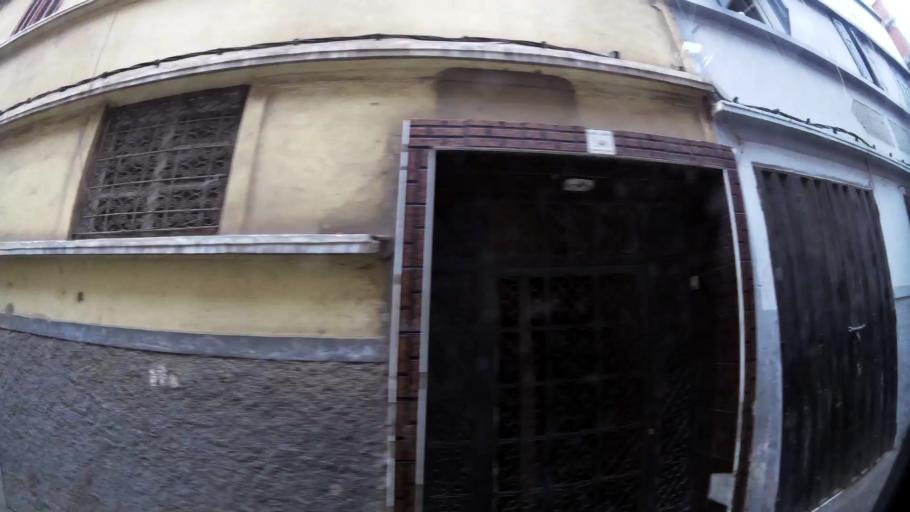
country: MA
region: Grand Casablanca
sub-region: Mediouna
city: Tit Mellil
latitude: 33.6123
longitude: -7.5092
